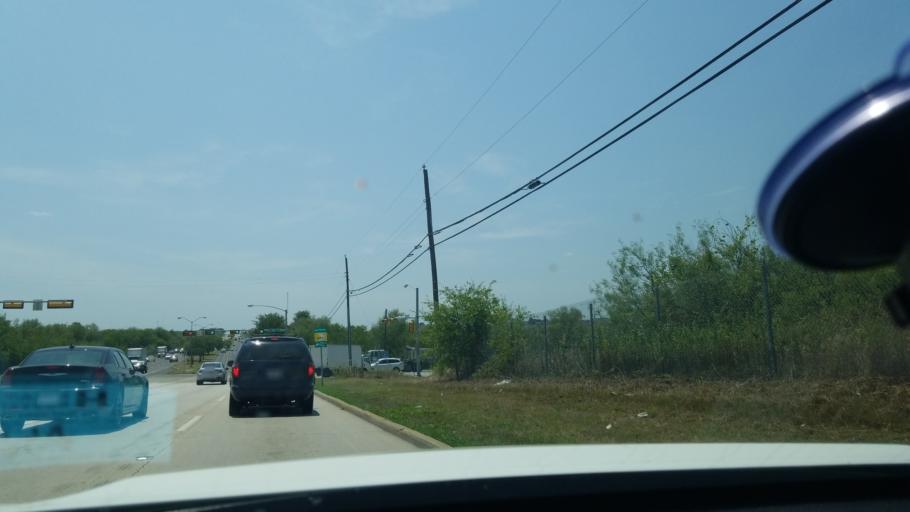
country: US
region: Texas
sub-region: Dallas County
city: Coppell
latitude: 32.8895
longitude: -96.9913
